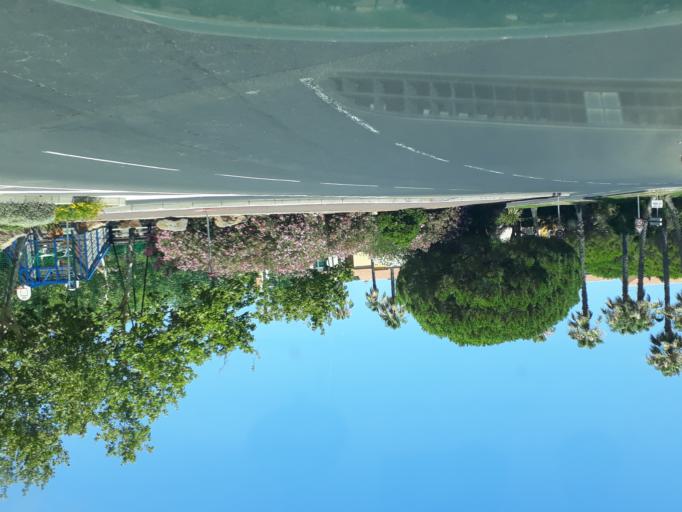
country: FR
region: Languedoc-Roussillon
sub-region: Departement de l'Herault
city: Le Cap d'Agde
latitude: 43.2825
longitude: 3.4989
